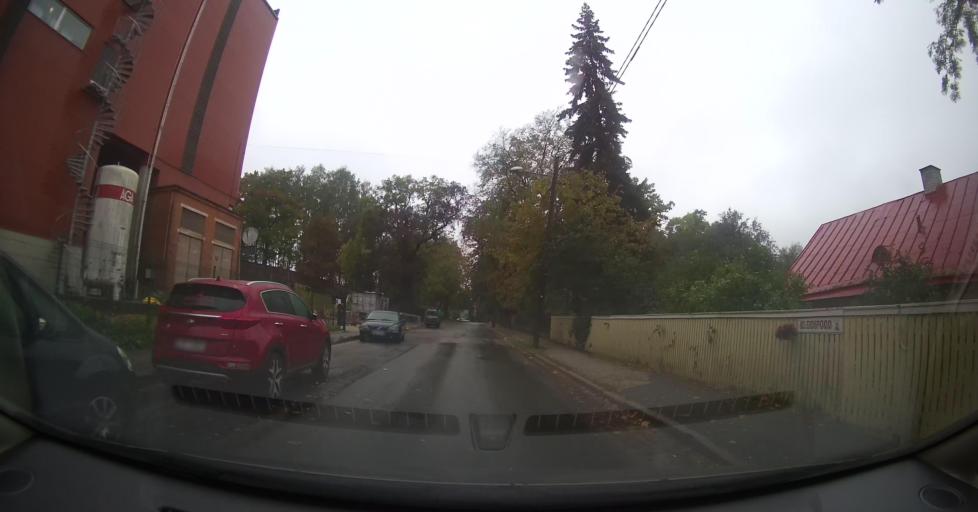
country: EE
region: Tartu
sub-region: Tartu linn
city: Tartu
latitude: 58.3869
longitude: 26.7065
